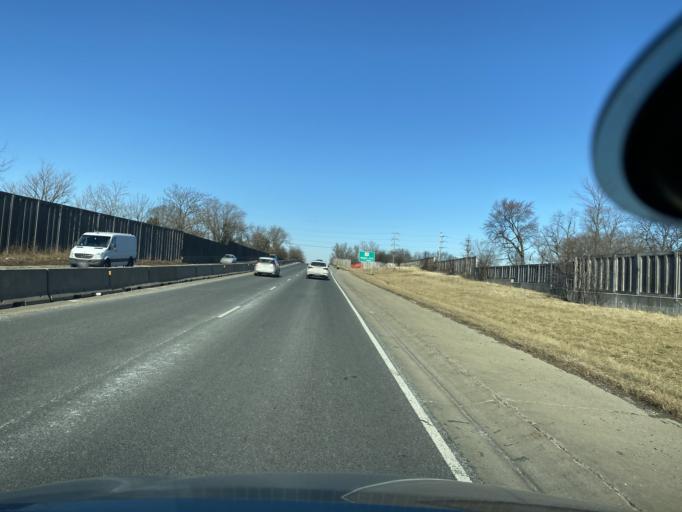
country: US
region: Illinois
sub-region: DuPage County
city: Clarendon Hills
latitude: 41.7972
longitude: -87.9466
